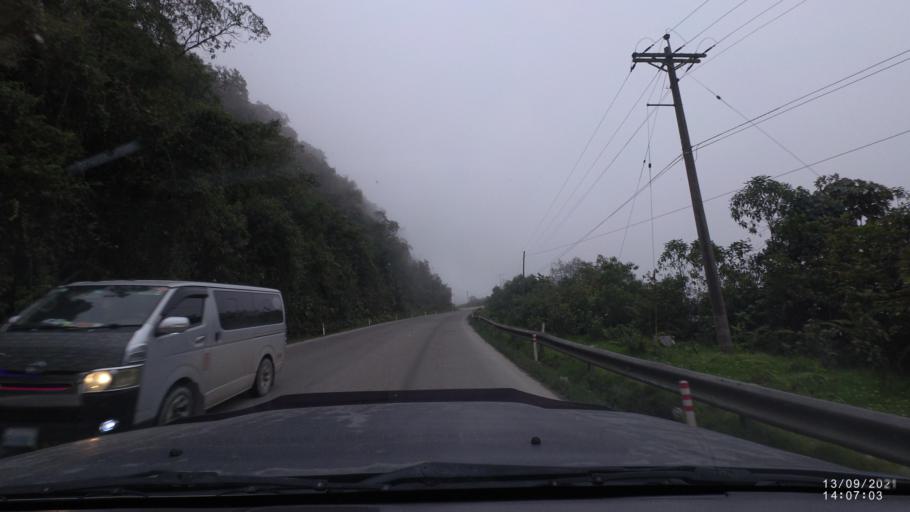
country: BO
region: Cochabamba
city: Colomi
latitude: -17.1831
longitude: -65.8867
